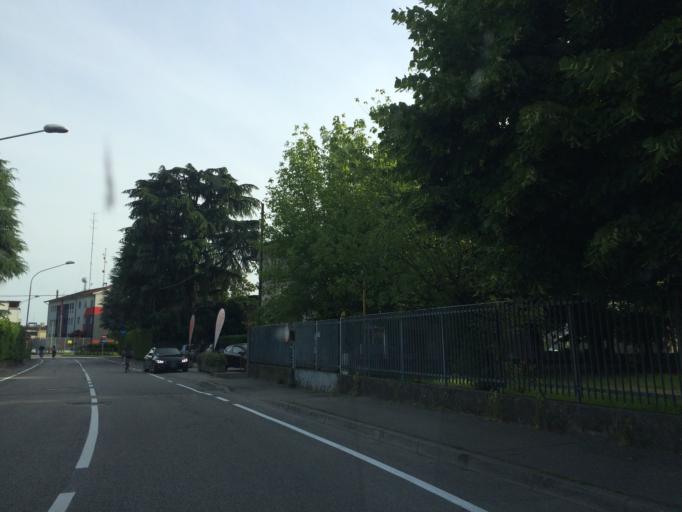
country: IT
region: Veneto
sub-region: Provincia di Padova
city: Cittadella
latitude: 45.6504
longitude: 11.7769
